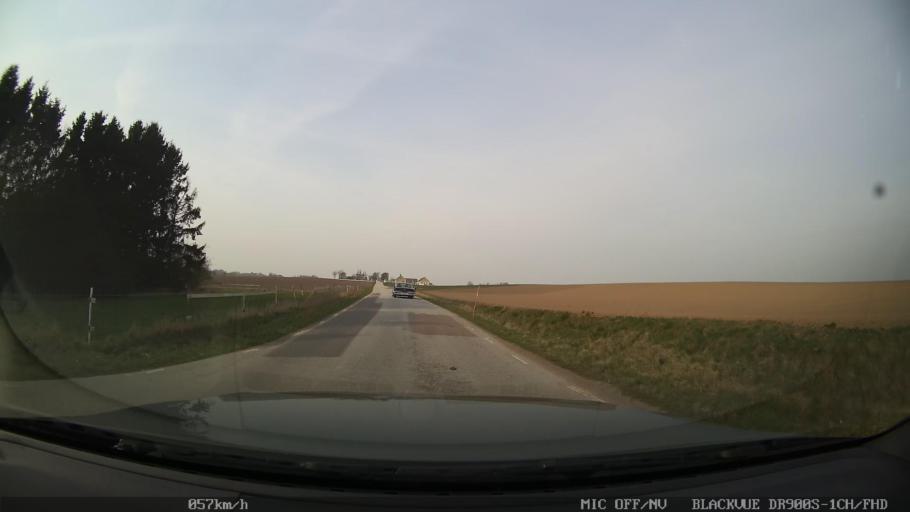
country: SE
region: Skane
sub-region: Ystads Kommun
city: Ystad
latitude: 55.4545
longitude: 13.8302
